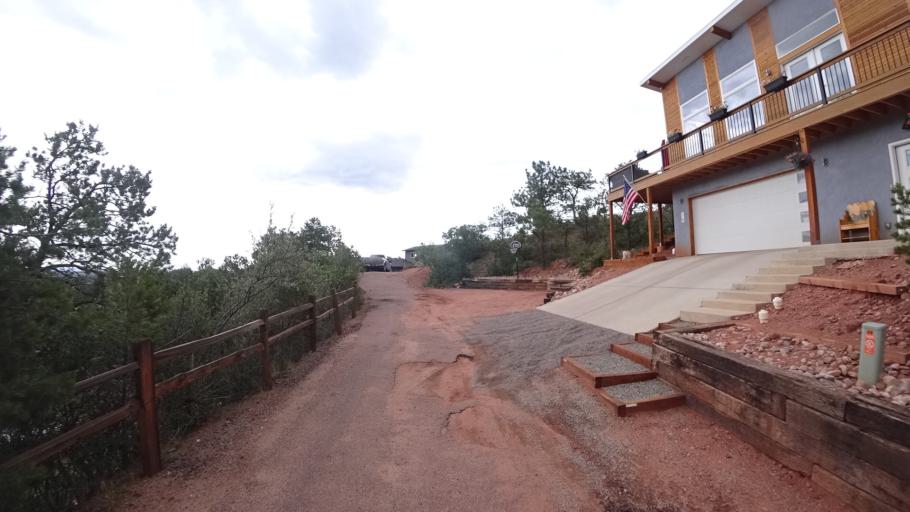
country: US
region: Colorado
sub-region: El Paso County
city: Manitou Springs
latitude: 38.8500
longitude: -104.8982
